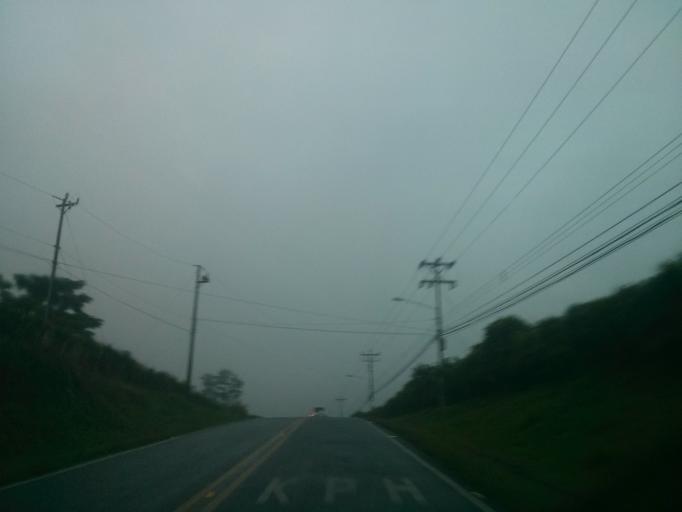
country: CR
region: Alajuela
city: Alajuela
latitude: 10.0432
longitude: -84.2098
